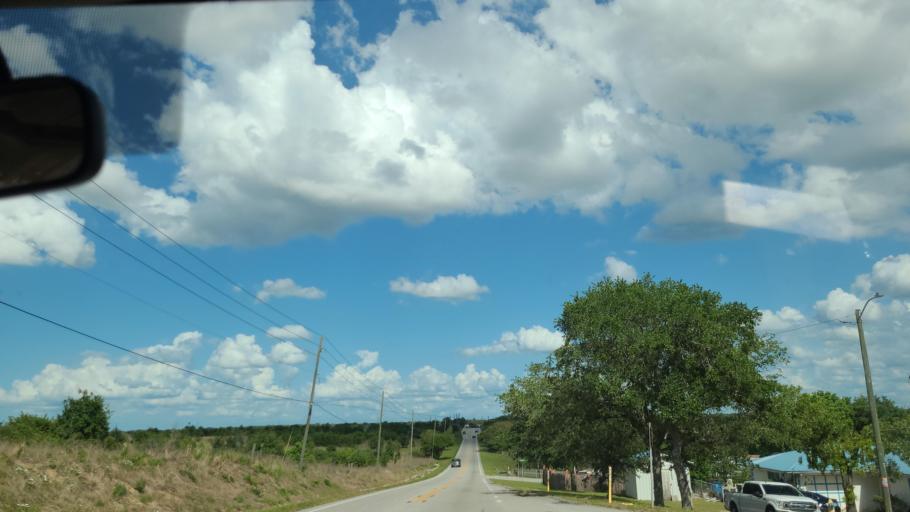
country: US
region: Florida
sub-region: Polk County
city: Lake Wales
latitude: 27.9140
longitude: -81.5605
